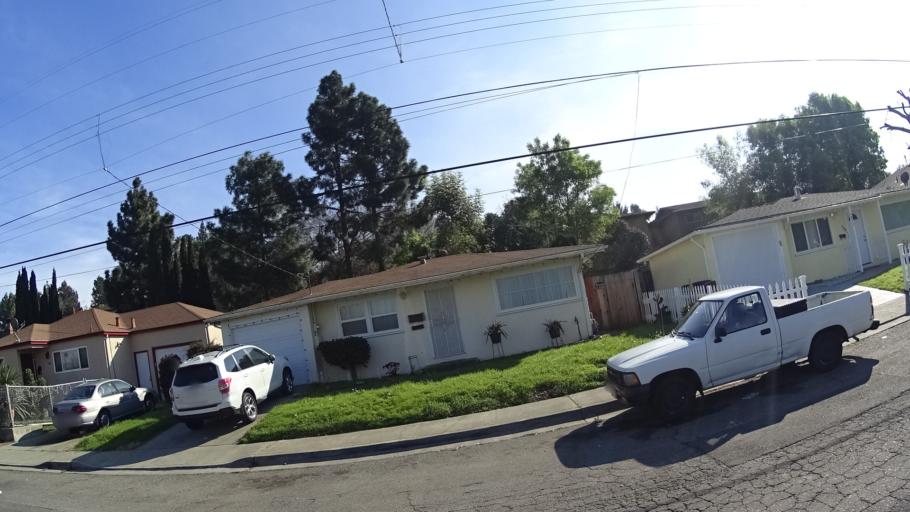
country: US
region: California
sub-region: Alameda County
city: Fairview
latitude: 37.6806
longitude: -122.0644
